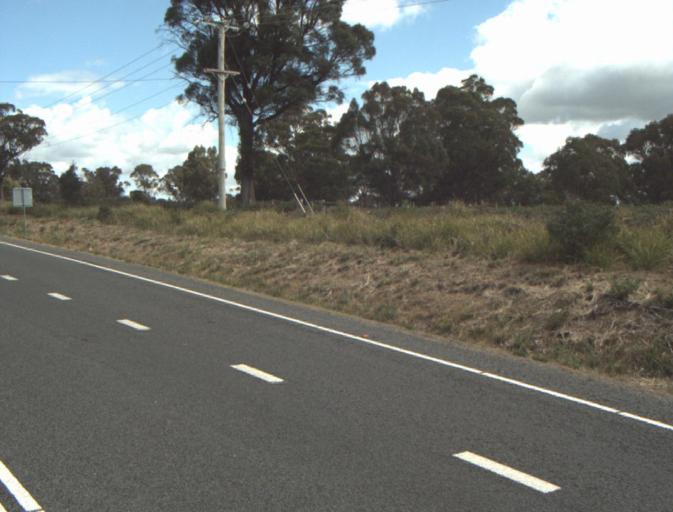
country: AU
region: Tasmania
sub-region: Launceston
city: Mayfield
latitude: -41.2767
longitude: 147.0372
